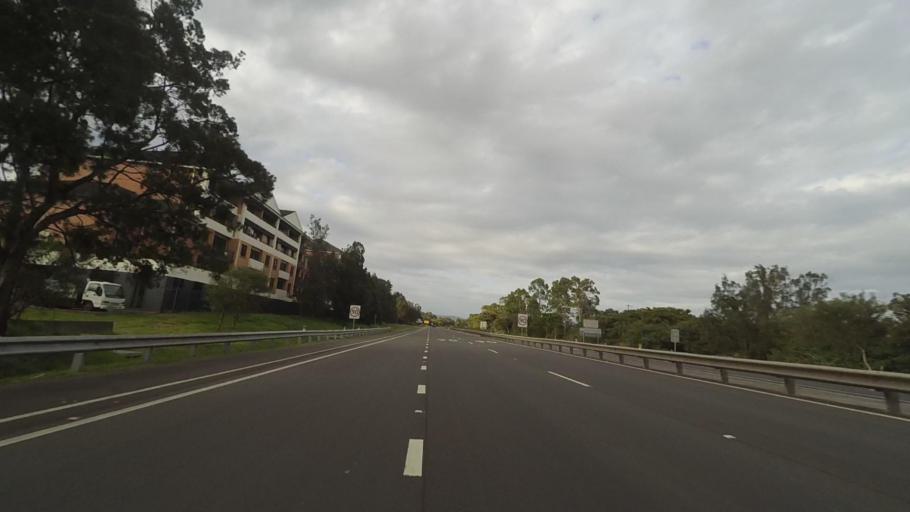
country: AU
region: New South Wales
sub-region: Wollongong
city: Fairy Meadow
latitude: -34.4039
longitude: 150.8926
